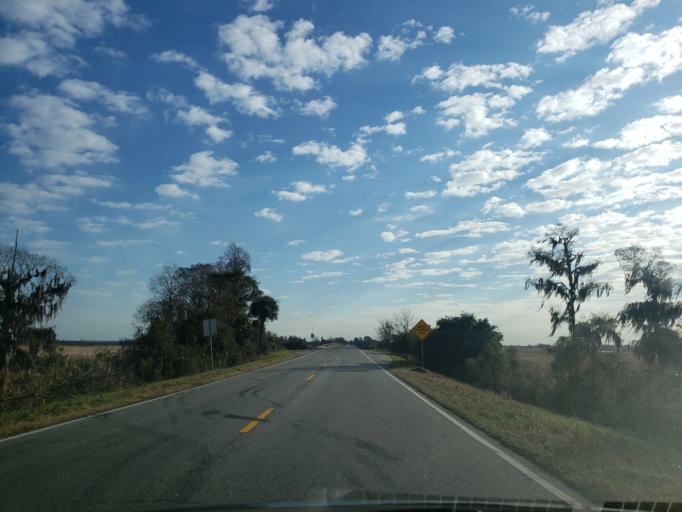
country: US
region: Georgia
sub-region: Chatham County
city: Port Wentworth
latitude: 32.1658
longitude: -81.1324
